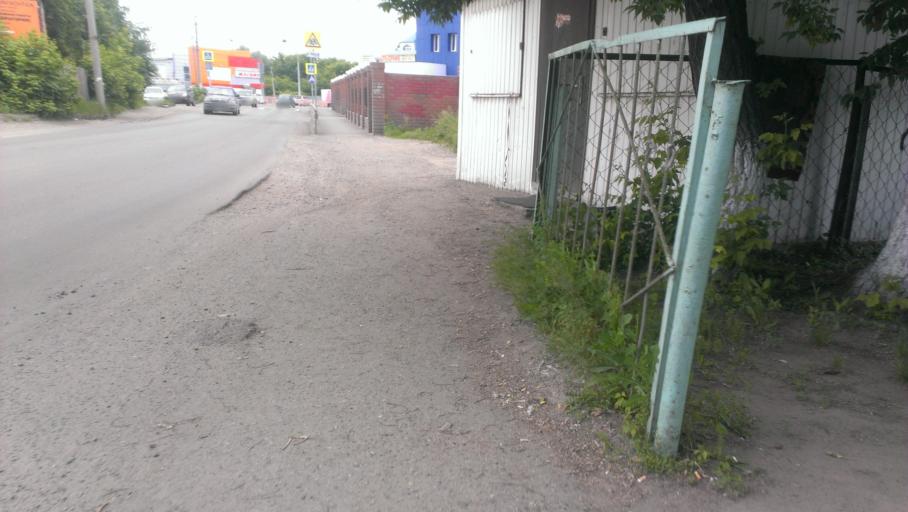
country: RU
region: Altai Krai
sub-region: Gorod Barnaulskiy
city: Barnaul
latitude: 53.3385
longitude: 83.7317
